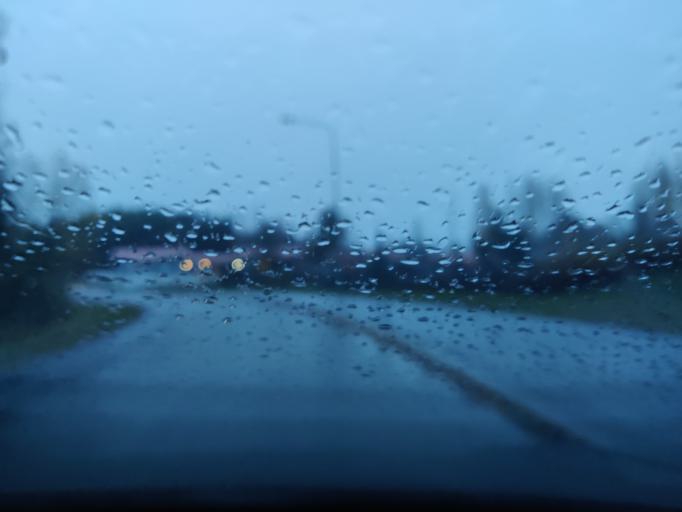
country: FI
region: Northern Savo
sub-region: Kuopio
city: Kuopio
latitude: 62.8312
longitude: 27.7156
